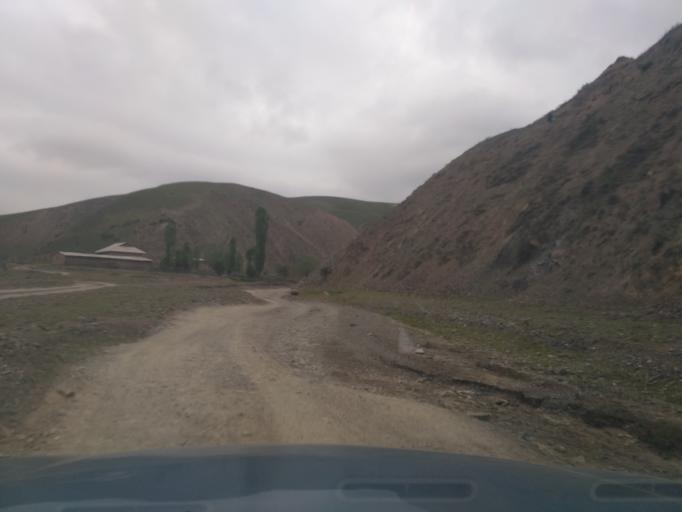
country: UZ
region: Jizzax
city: Zomin
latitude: 39.8466
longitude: 68.3999
